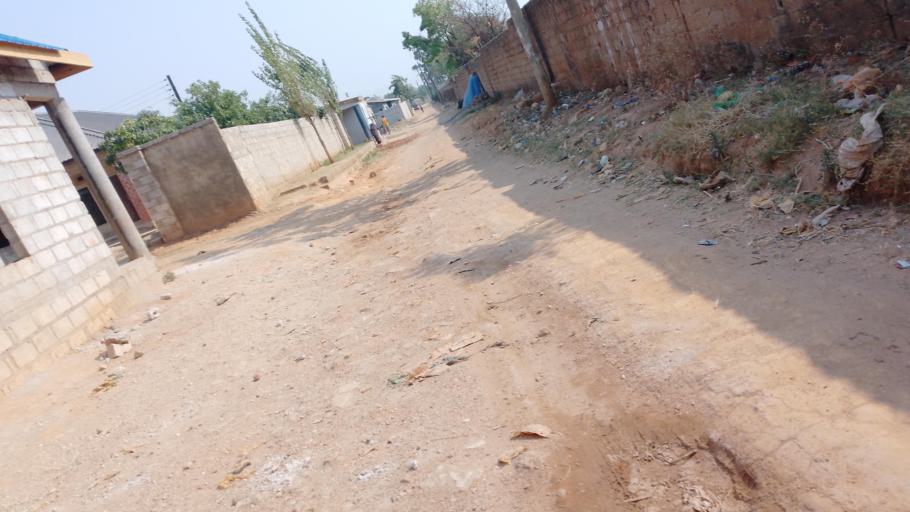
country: ZM
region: Lusaka
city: Lusaka
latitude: -15.4044
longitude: 28.3835
